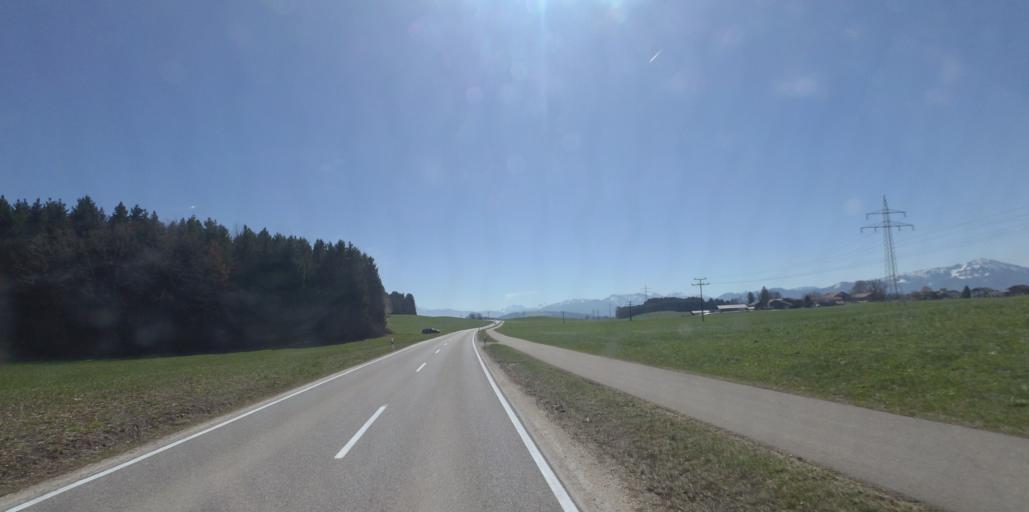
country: DE
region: Bavaria
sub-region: Upper Bavaria
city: Nussdorf
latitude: 47.8928
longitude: 12.6103
